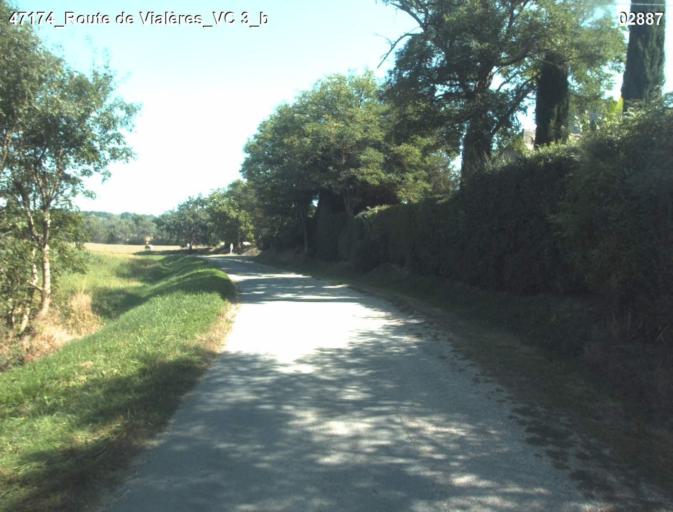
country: FR
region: Aquitaine
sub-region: Departement du Lot-et-Garonne
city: Nerac
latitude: 44.0581
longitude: 0.3864
